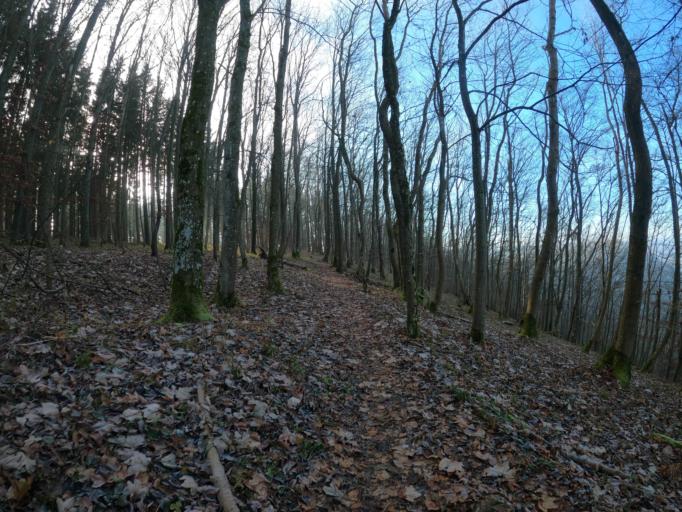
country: DE
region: Baden-Wuerttemberg
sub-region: Regierungsbezirk Stuttgart
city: Deggingen
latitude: 48.5900
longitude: 9.7396
